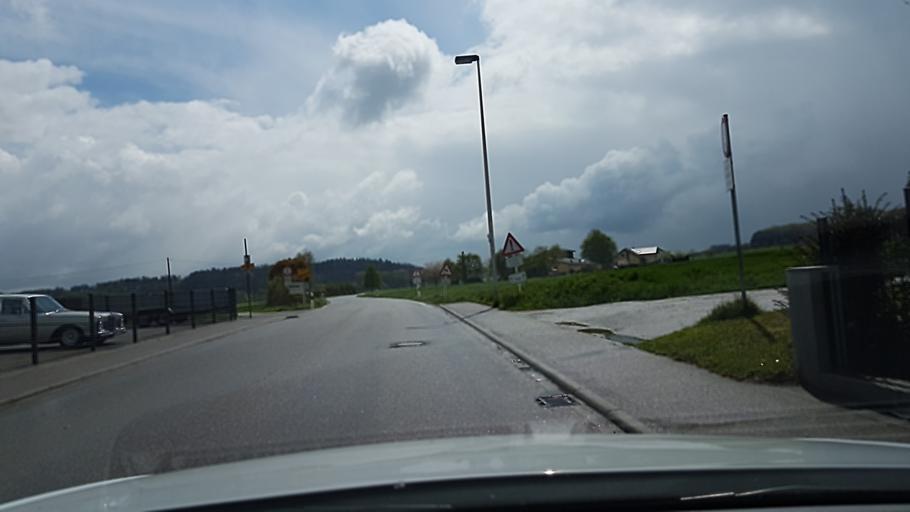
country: DE
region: Baden-Wuerttemberg
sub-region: Regierungsbezirk Stuttgart
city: Aspach
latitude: 48.9883
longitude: 9.3643
